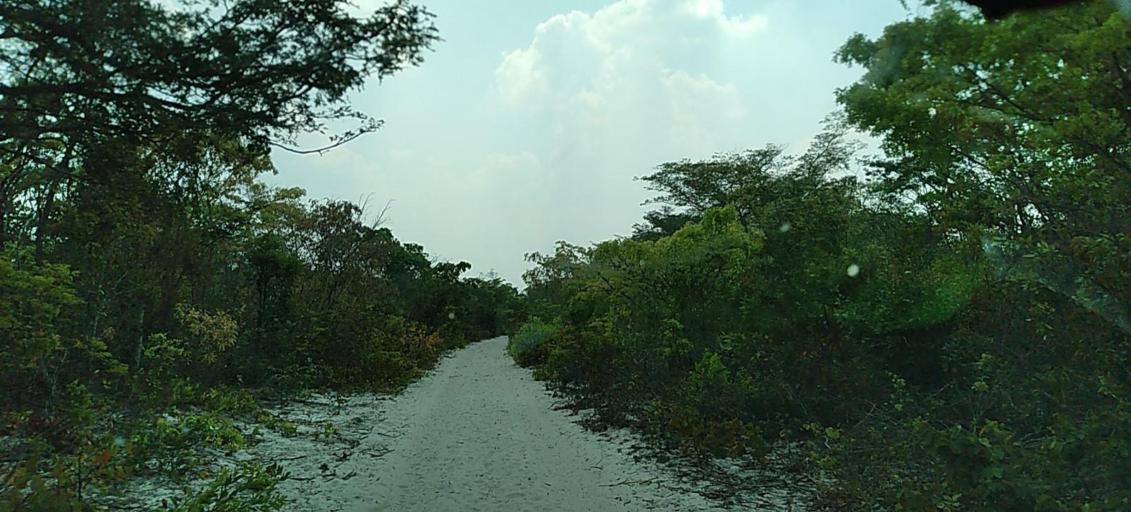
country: ZM
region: North-Western
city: Kabompo
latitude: -13.4007
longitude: 23.8125
